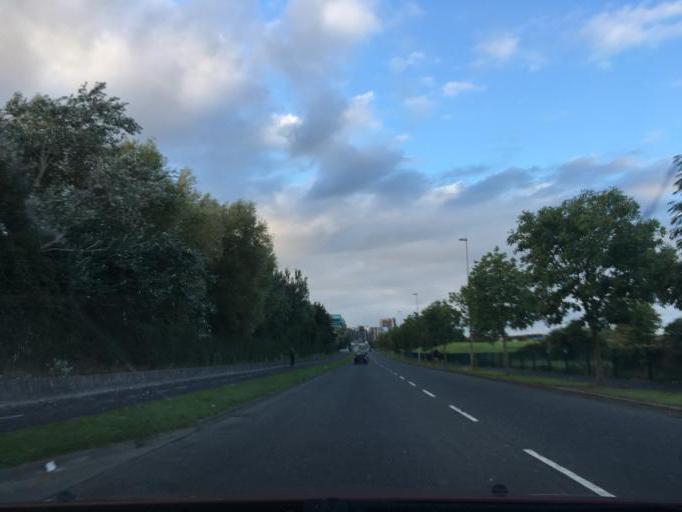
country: IE
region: Leinster
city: Oldbawn
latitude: 53.2786
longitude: -6.3740
